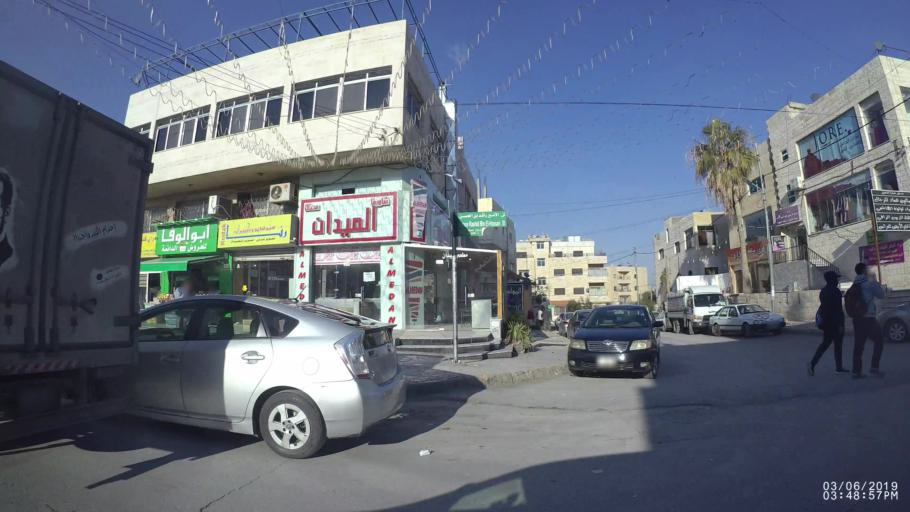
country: JO
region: Amman
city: Amman
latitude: 31.9723
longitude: 35.9511
